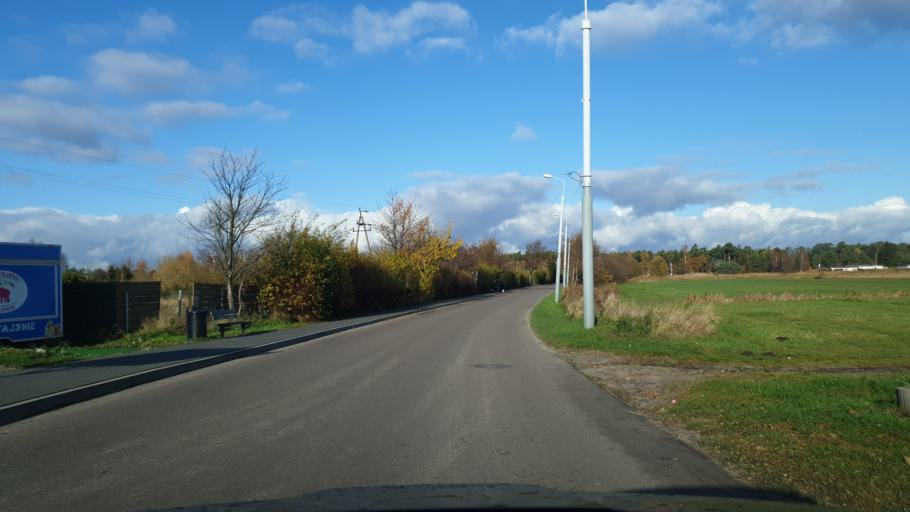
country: PL
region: Pomeranian Voivodeship
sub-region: Powiat pucki
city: Jastrzebia Gora
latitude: 54.8258
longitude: 18.2440
